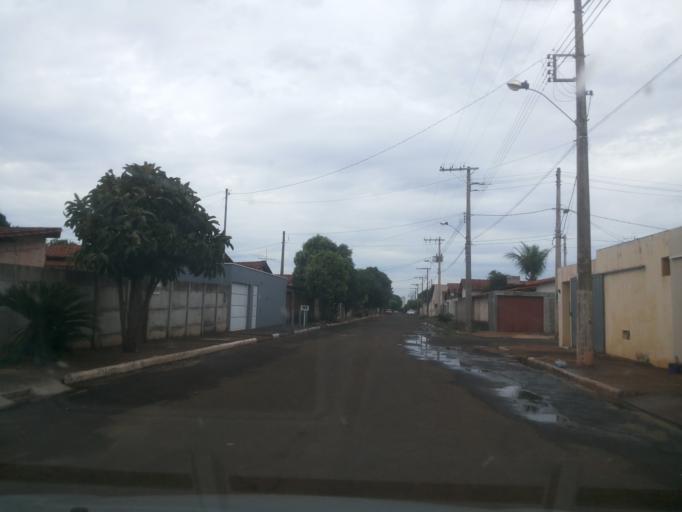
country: BR
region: Minas Gerais
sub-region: Ituiutaba
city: Ituiutaba
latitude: -18.9757
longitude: -49.4802
